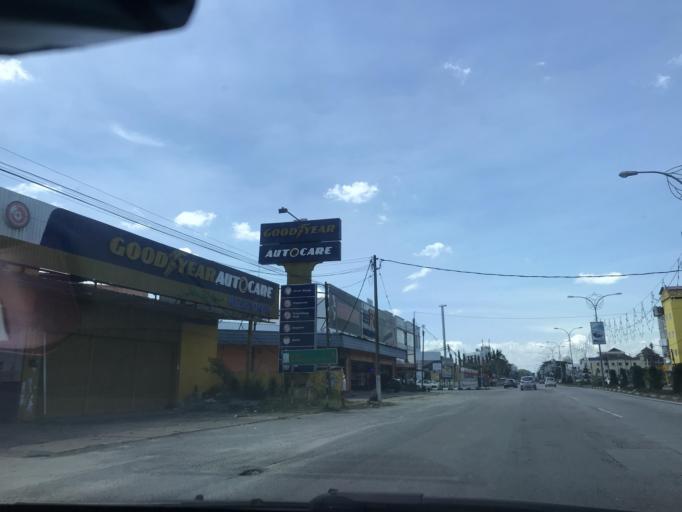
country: MY
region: Kelantan
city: Kota Bharu
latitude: 6.1073
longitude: 102.2577
